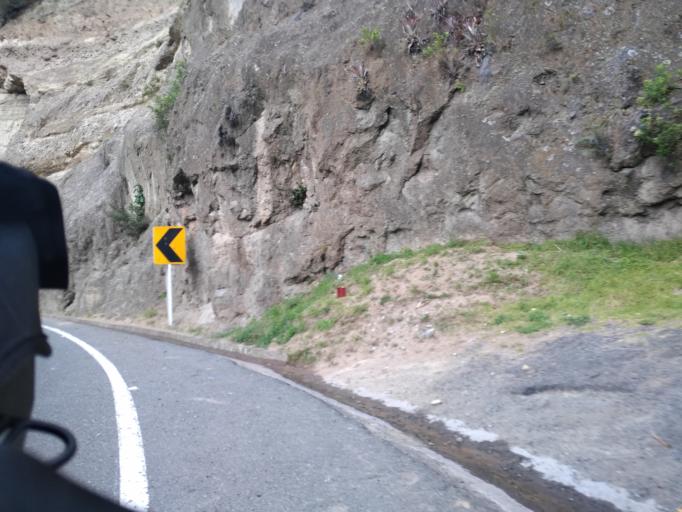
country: CO
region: Narino
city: Funes
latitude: 0.9482
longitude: -77.4740
